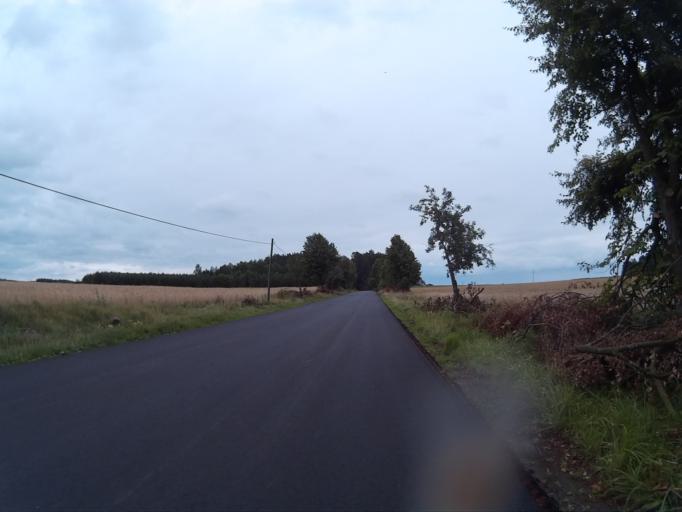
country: PL
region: Kujawsko-Pomorskie
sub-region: Powiat swiecki
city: Lniano
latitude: 53.6041
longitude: 18.2253
